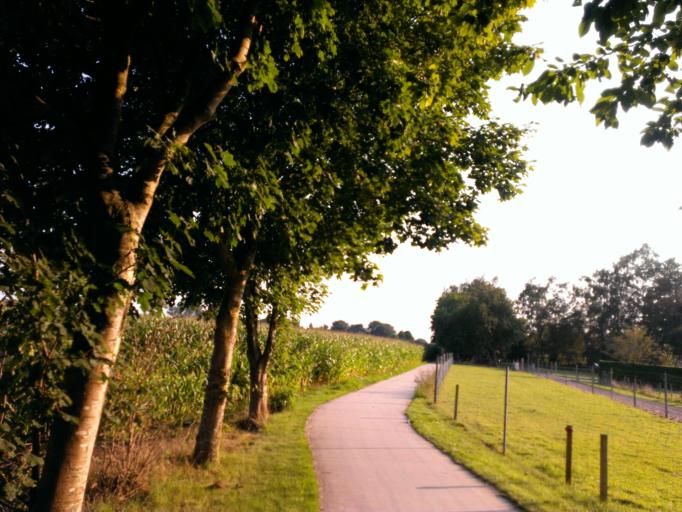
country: NL
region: Gelderland
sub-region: Gemeente Heerde
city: Heerde
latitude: 52.4126
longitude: 6.0615
